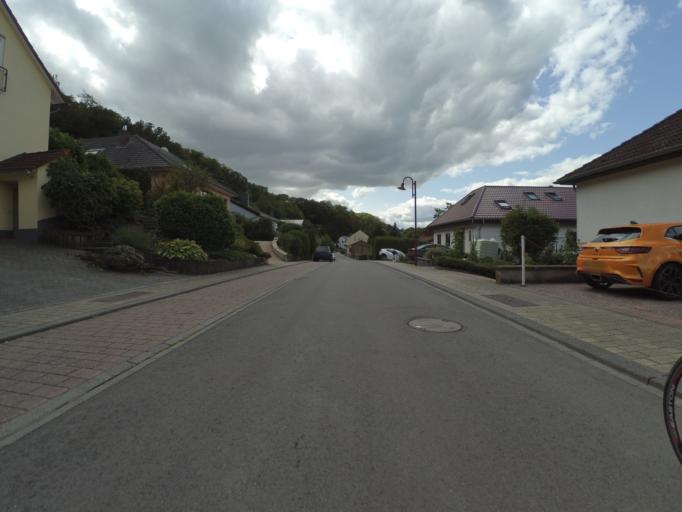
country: LU
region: Grevenmacher
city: Gonderange
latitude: 49.6809
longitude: 6.2508
